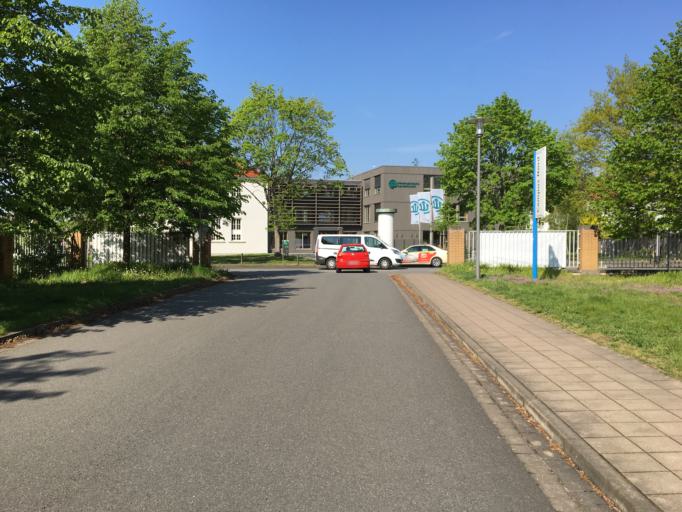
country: DE
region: Lower Saxony
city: Braunschweig
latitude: 52.2837
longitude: 10.5385
